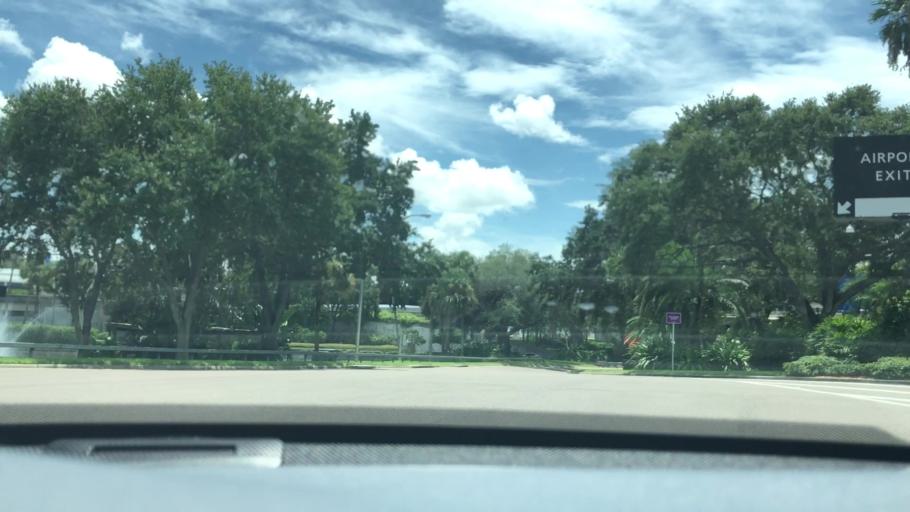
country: US
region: Florida
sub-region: Hillsborough County
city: Egypt Lake-Leto
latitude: 27.9765
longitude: -82.5357
